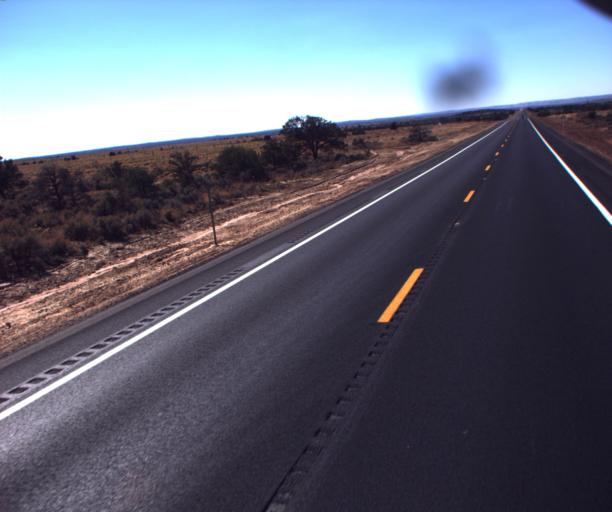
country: US
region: Arizona
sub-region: Apache County
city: Ganado
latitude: 35.7181
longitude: -109.3947
